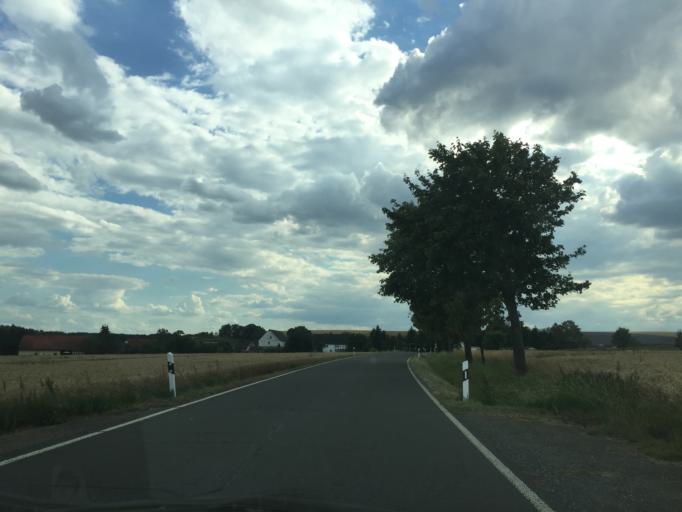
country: DE
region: Thuringia
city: Saara
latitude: 50.9437
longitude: 12.4179
